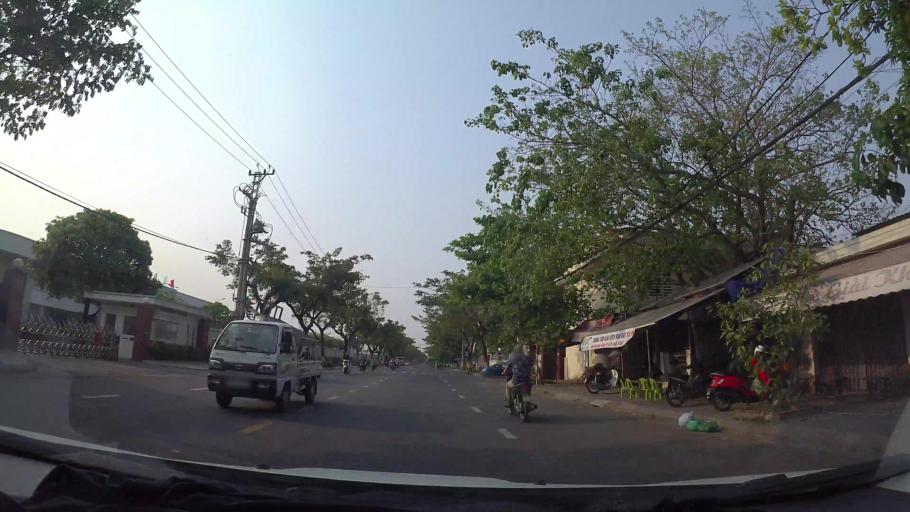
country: VN
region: Da Nang
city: Cam Le
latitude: 16.0193
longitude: 108.2036
